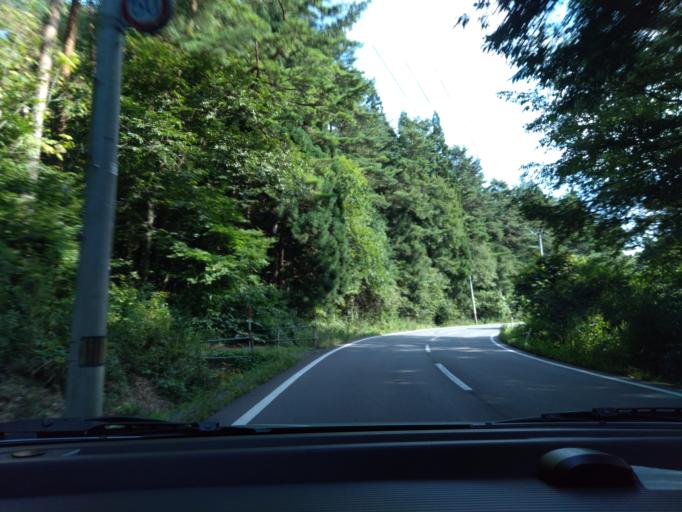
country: JP
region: Iwate
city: Morioka-shi
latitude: 39.5953
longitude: 141.0895
